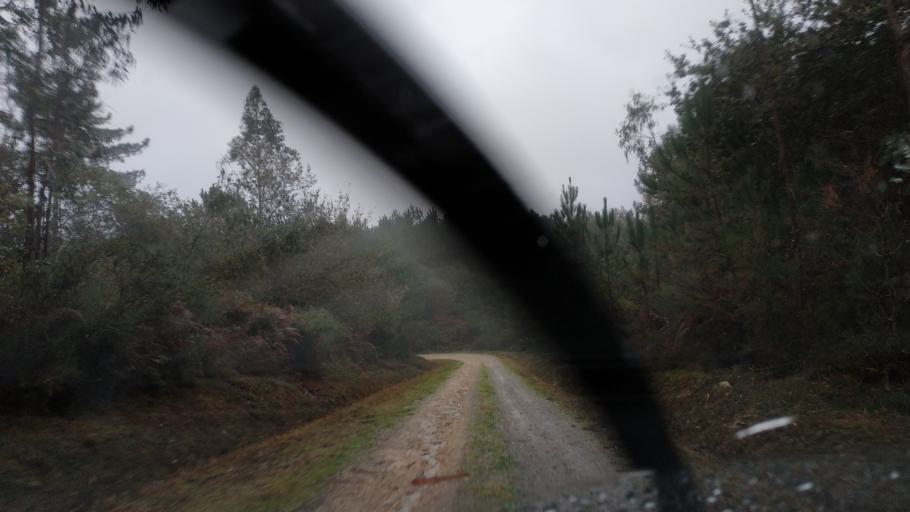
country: ES
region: Galicia
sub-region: Provincia da Coruna
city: Negreira
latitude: 42.9072
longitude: -8.7654
